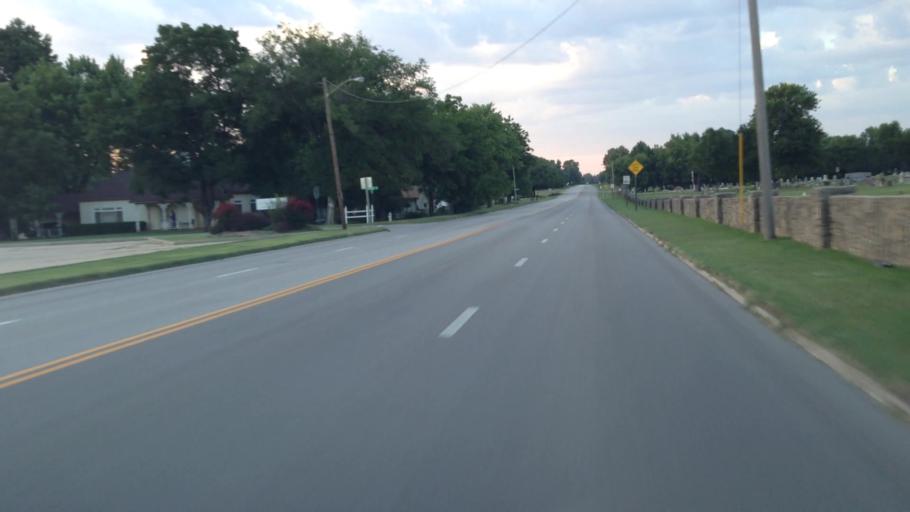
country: US
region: Kansas
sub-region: Montgomery County
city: Independence
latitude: 37.2465
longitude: -95.7062
